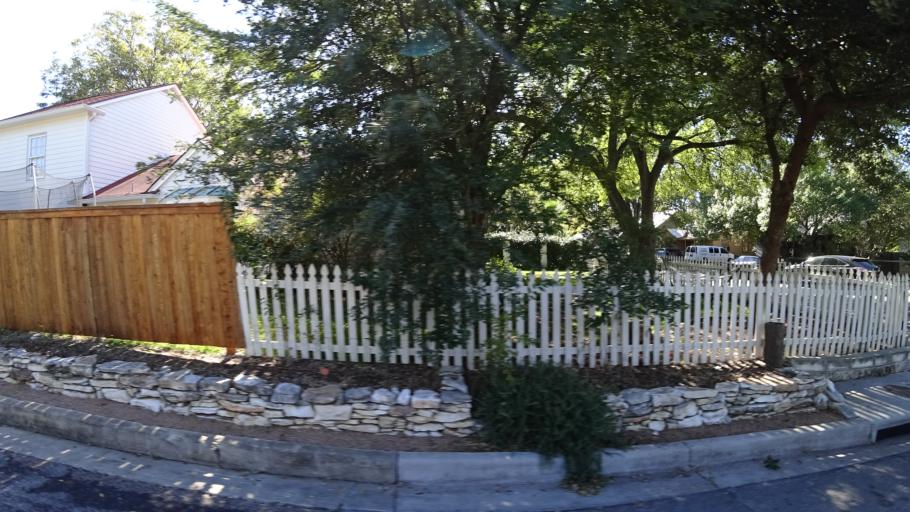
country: US
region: Texas
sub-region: Travis County
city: Austin
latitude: 30.3184
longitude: -97.7442
